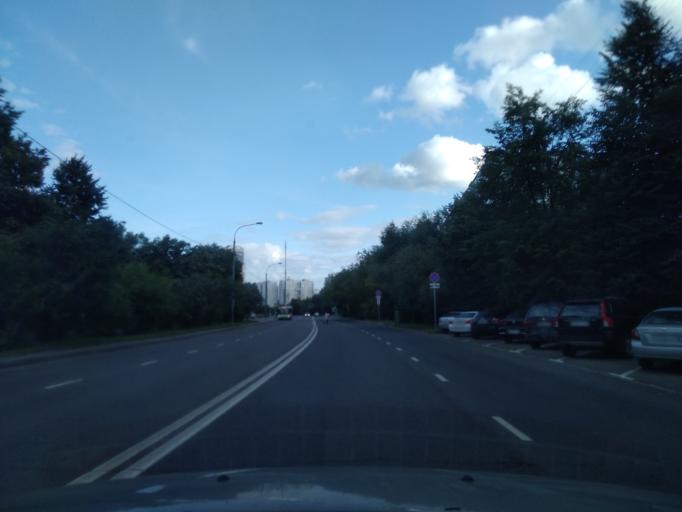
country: RU
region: Moscow
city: Strogino
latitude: 55.8117
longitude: 37.4120
